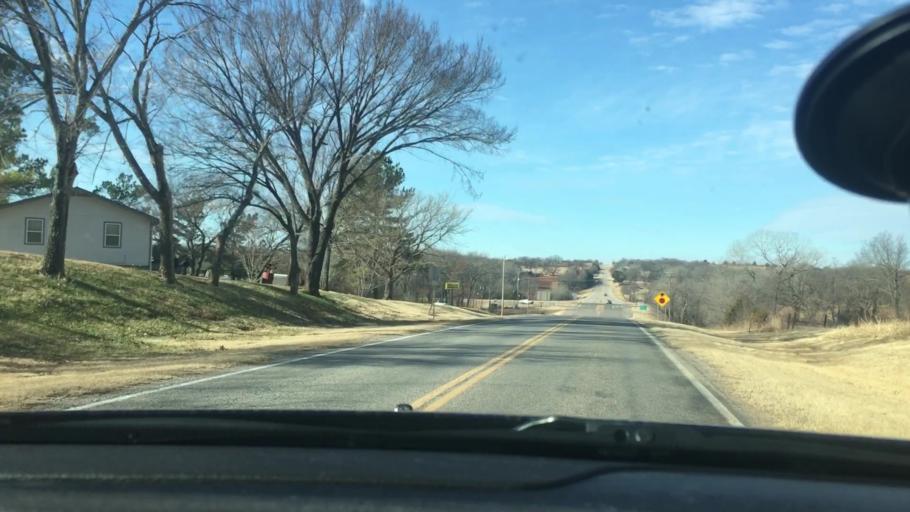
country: US
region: Oklahoma
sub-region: Seminole County
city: Konawa
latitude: 34.9859
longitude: -96.9258
